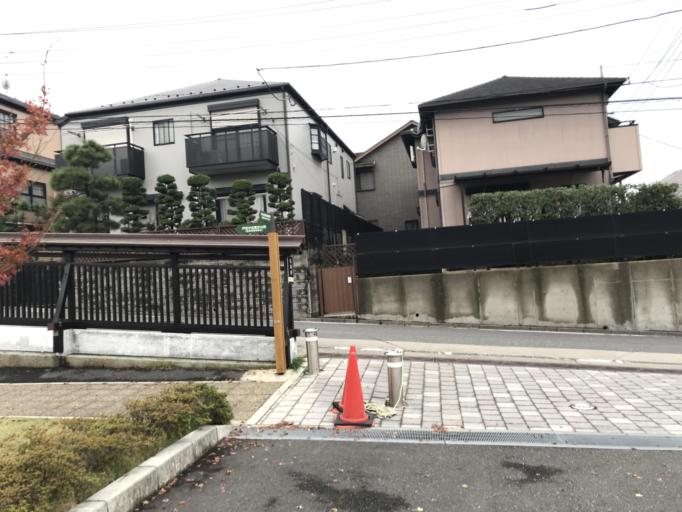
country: JP
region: Chiba
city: Matsudo
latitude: 35.7787
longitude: 139.8997
